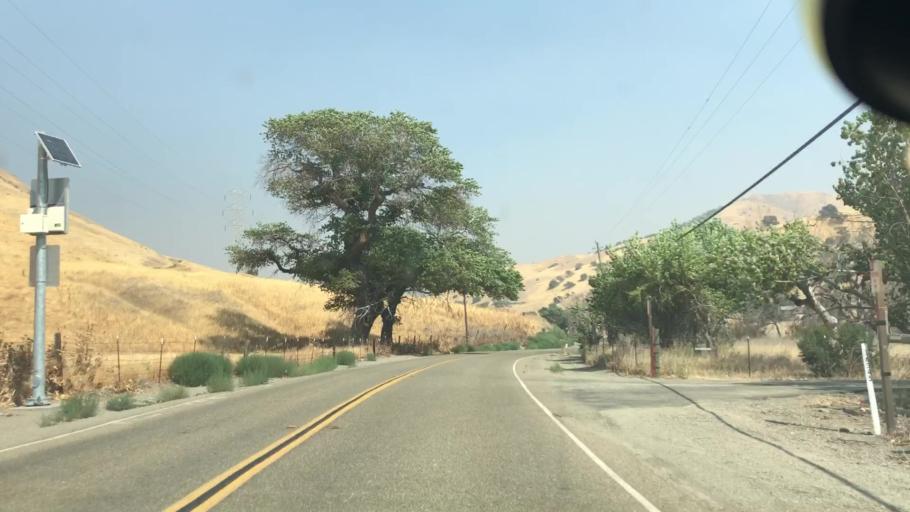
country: US
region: California
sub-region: San Joaquin County
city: Mountain House
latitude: 37.6398
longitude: -121.5866
